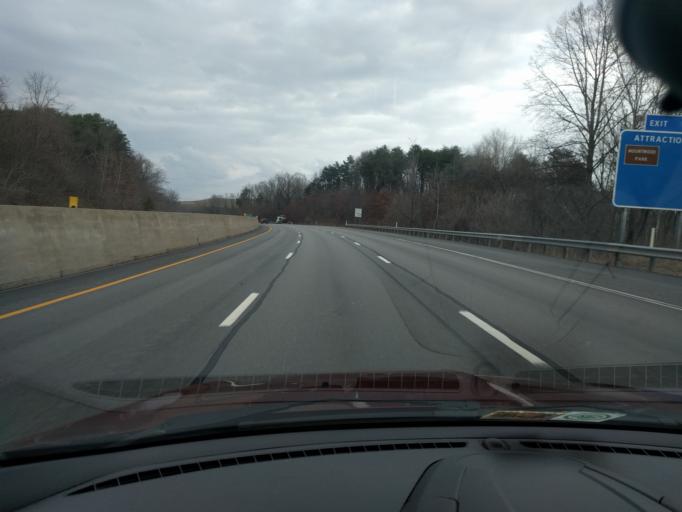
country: US
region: West Virginia
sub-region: Wood County
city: Mineral Wells
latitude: 39.2391
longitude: -81.5013
